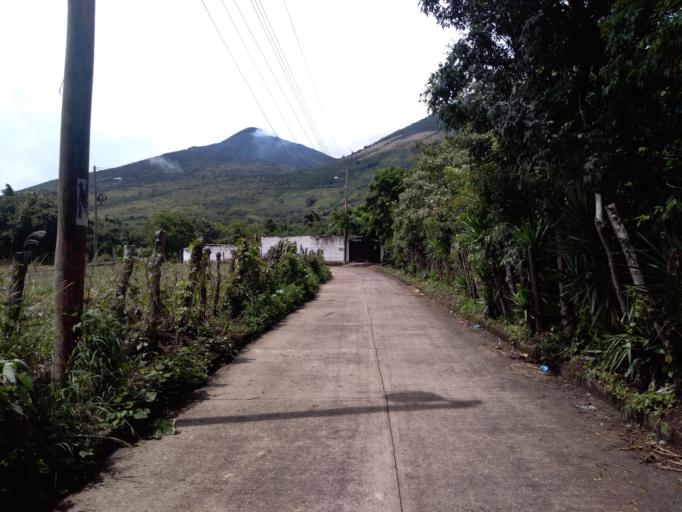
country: GT
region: Escuintla
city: San Vicente Pacaya
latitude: 14.3688
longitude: -90.5647
